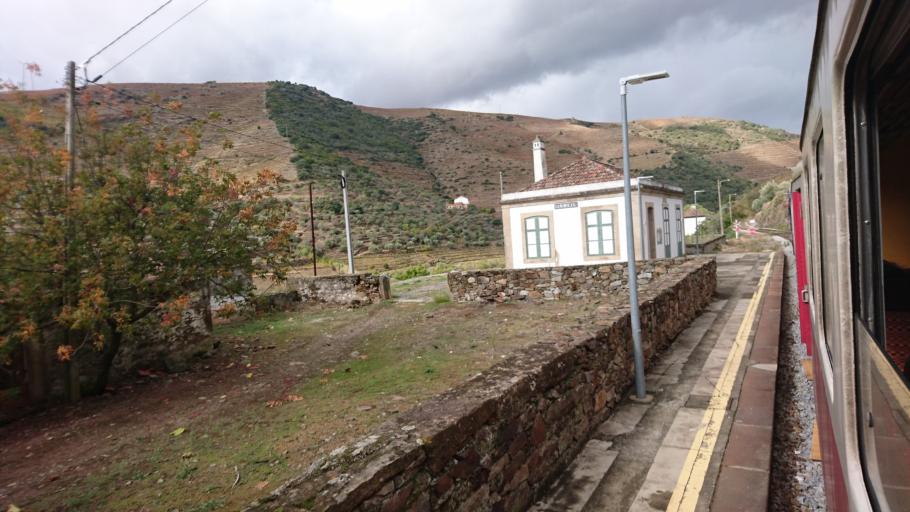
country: PT
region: Viseu
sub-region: Sao Joao da Pesqueira
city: Sao Joao da Pesqueira
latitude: 41.1758
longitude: -7.3774
